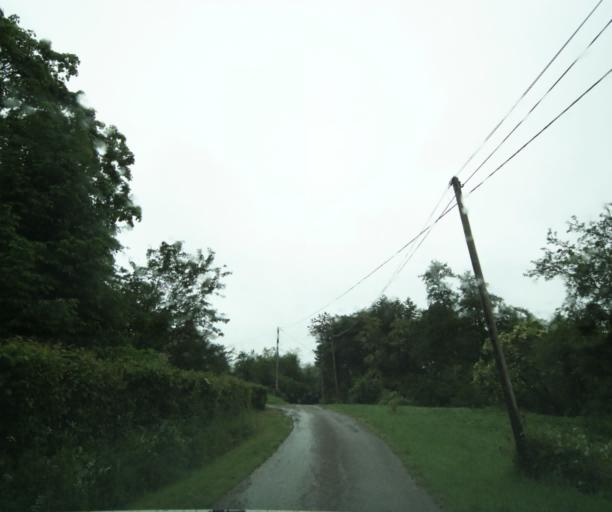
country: FR
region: Bourgogne
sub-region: Departement de Saone-et-Loire
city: Matour
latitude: 46.3680
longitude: 4.3875
